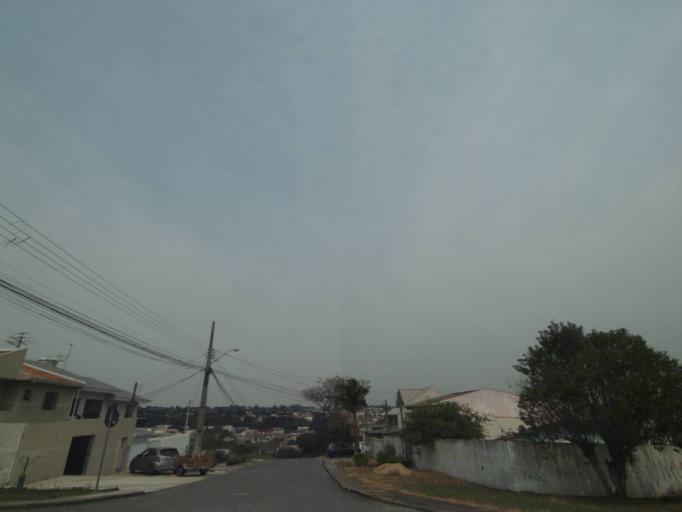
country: BR
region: Parana
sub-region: Sao Jose Dos Pinhais
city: Sao Jose dos Pinhais
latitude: -25.5198
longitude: -49.2808
